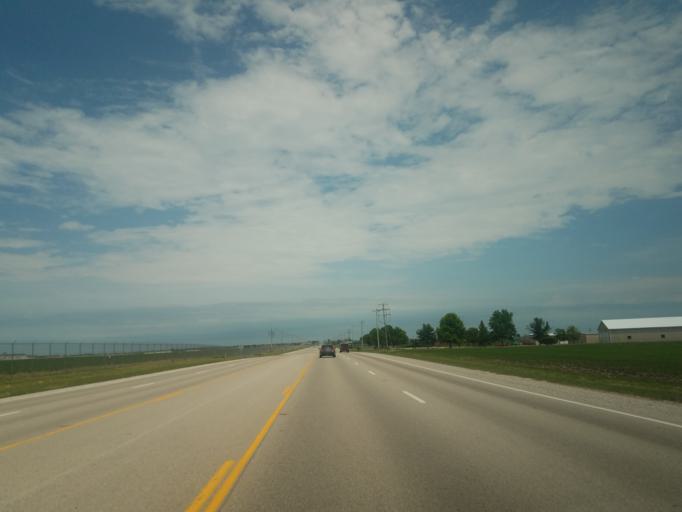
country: US
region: Illinois
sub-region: McLean County
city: Downs
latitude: 40.4761
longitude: -88.9023
